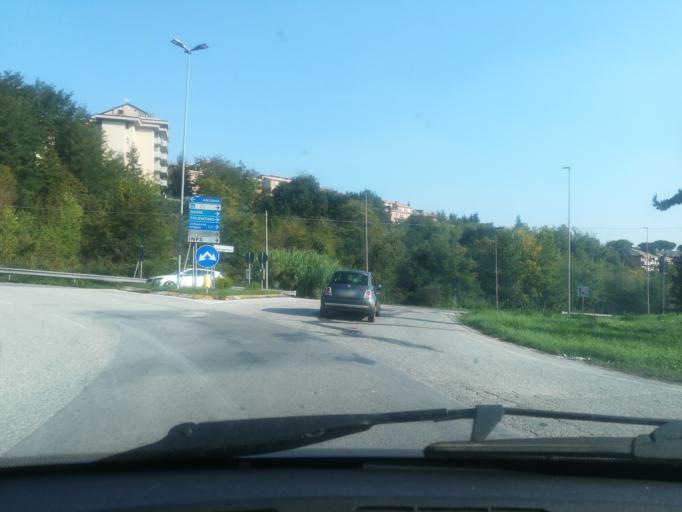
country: IT
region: The Marches
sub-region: Provincia di Macerata
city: Macerata
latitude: 43.2952
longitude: 13.4422
